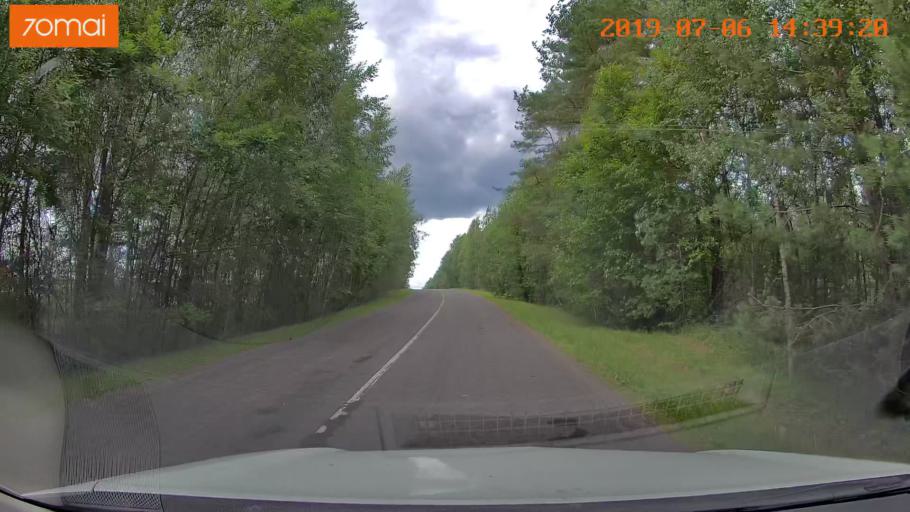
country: BY
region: Minsk
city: Ivyanyets
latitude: 53.9156
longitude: 26.6905
